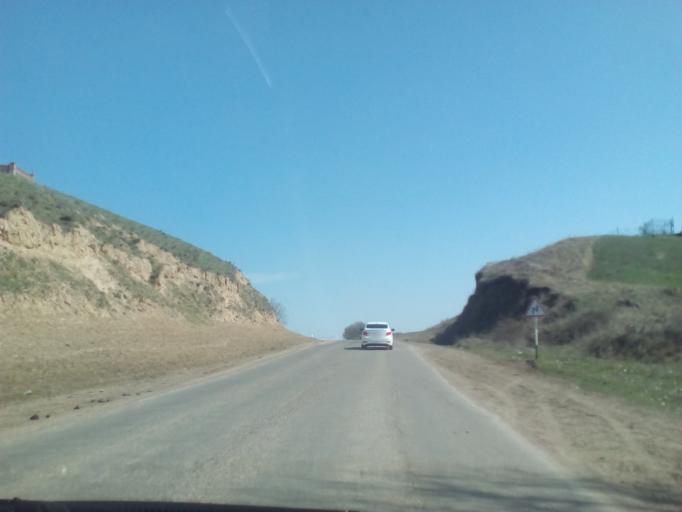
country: KZ
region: Almaty Oblysy
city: Burunday
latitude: 43.1795
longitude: 76.4187
